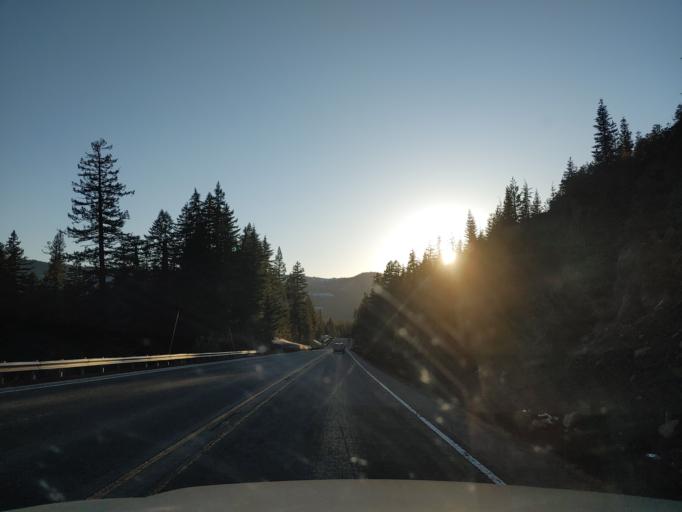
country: US
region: Oregon
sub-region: Lane County
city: Oakridge
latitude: 43.6115
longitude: -122.1100
